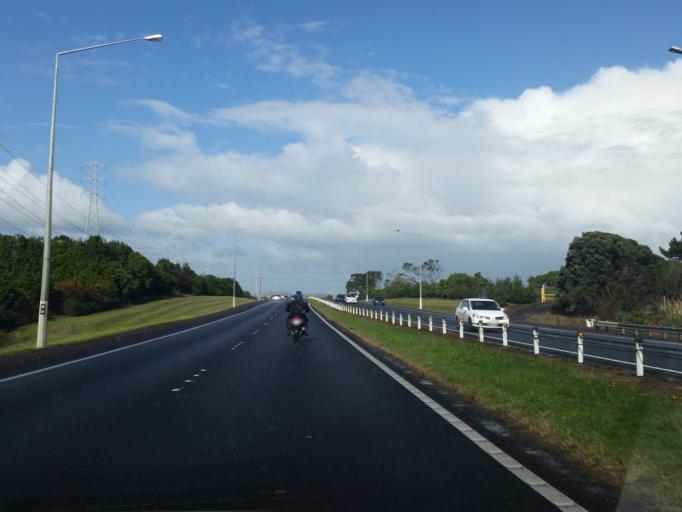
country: NZ
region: Auckland
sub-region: Auckland
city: Takanini
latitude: -37.0524
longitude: 174.9183
